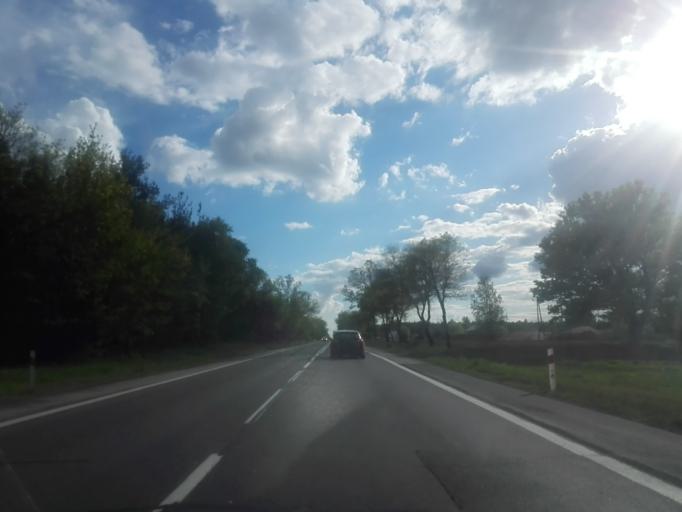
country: PL
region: Masovian Voivodeship
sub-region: Powiat wyszkowski
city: Dlugosiodlo
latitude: 52.7158
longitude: 21.7008
